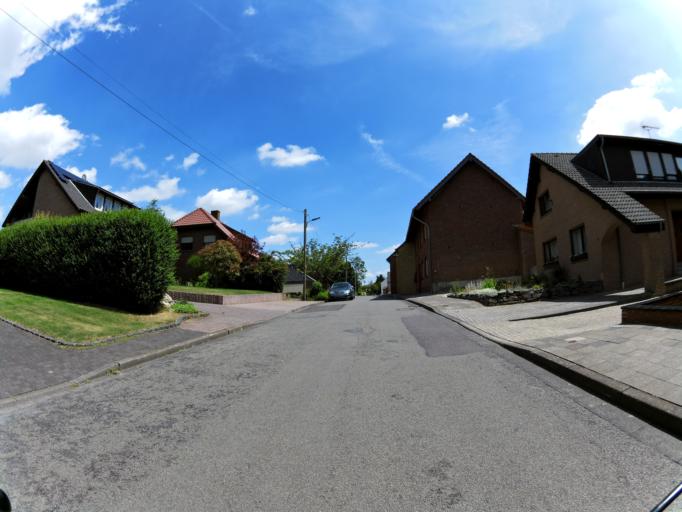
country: NL
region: Limburg
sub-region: Gemeente Echt-Susteren
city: Koningsbosch
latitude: 51.0270
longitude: 5.9843
